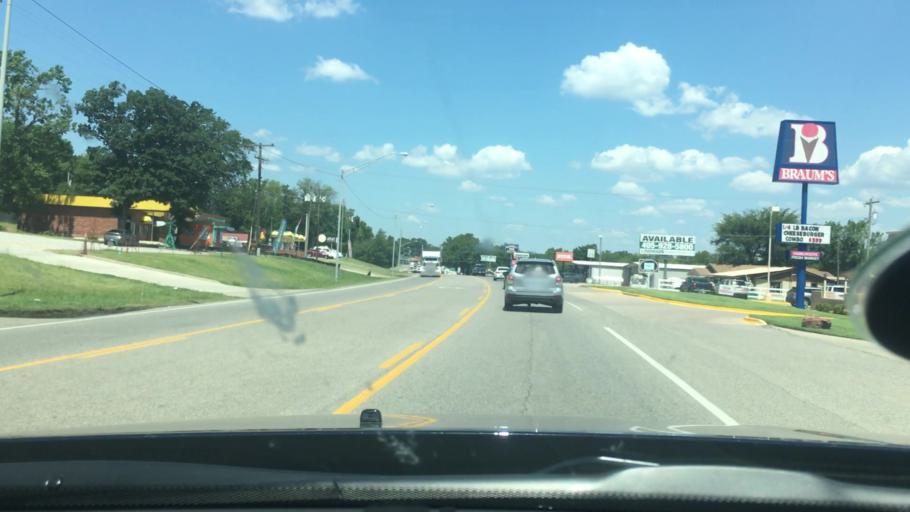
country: US
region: Oklahoma
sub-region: Marshall County
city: Madill
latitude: 34.0800
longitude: -96.7645
